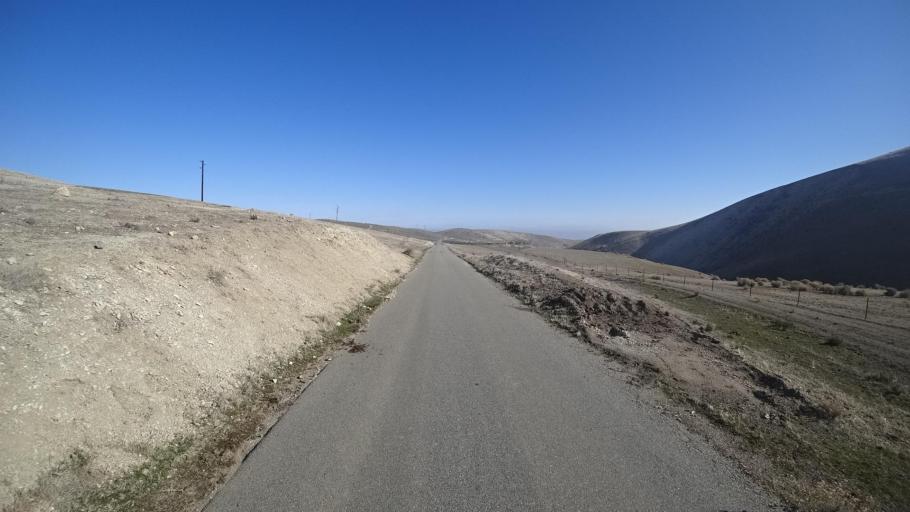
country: US
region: California
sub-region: Kern County
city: Taft Heights
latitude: 35.2303
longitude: -119.6658
